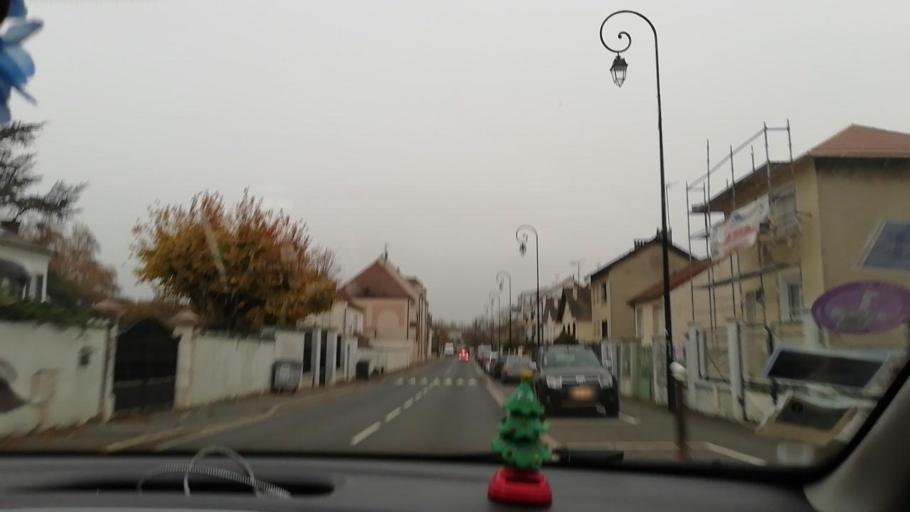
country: FR
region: Ile-de-France
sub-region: Departement de Seine-et-Marne
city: Claye-Souilly
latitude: 48.9437
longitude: 2.6866
